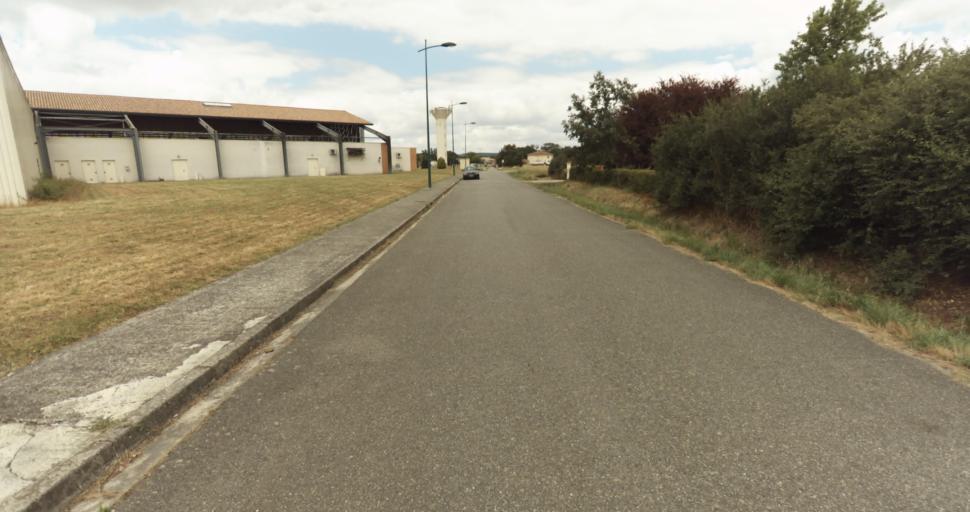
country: FR
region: Midi-Pyrenees
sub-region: Departement de la Haute-Garonne
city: Fontenilles
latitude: 43.5475
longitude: 1.1942
